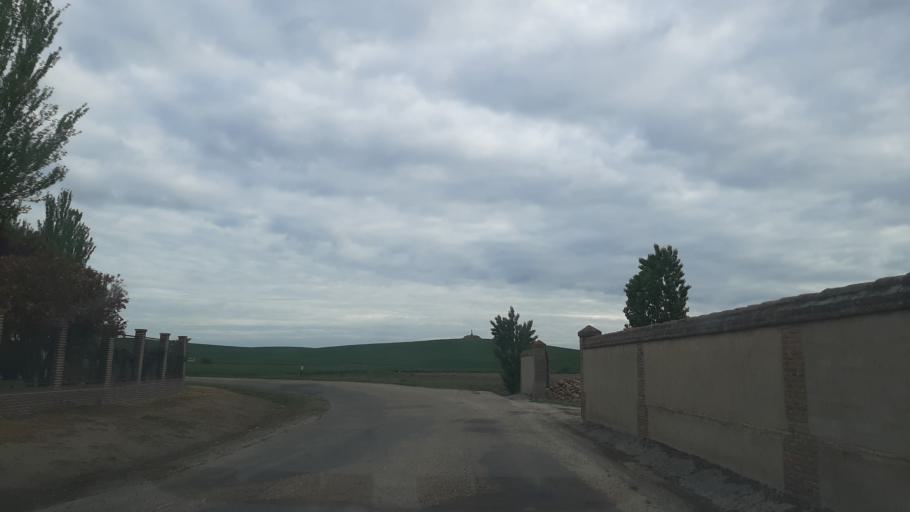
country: ES
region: Castille and Leon
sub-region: Provincia de Salamanca
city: Palaciosrubios
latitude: 41.0560
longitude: -5.1960
